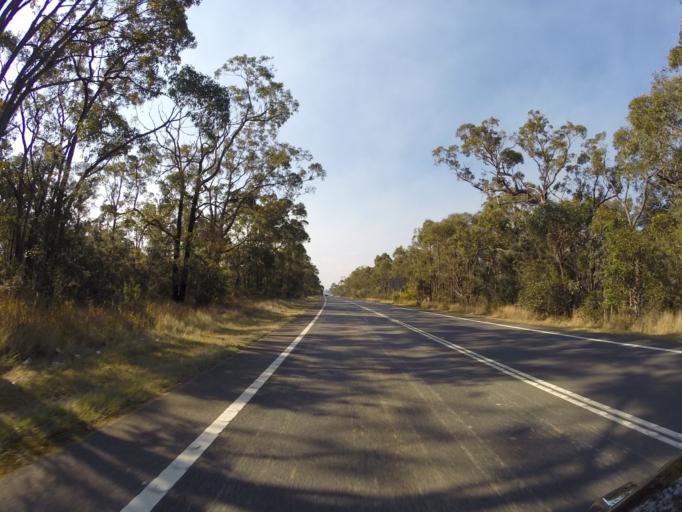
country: AU
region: New South Wales
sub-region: Sutherland Shire
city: Menai
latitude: -34.0152
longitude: 150.9831
